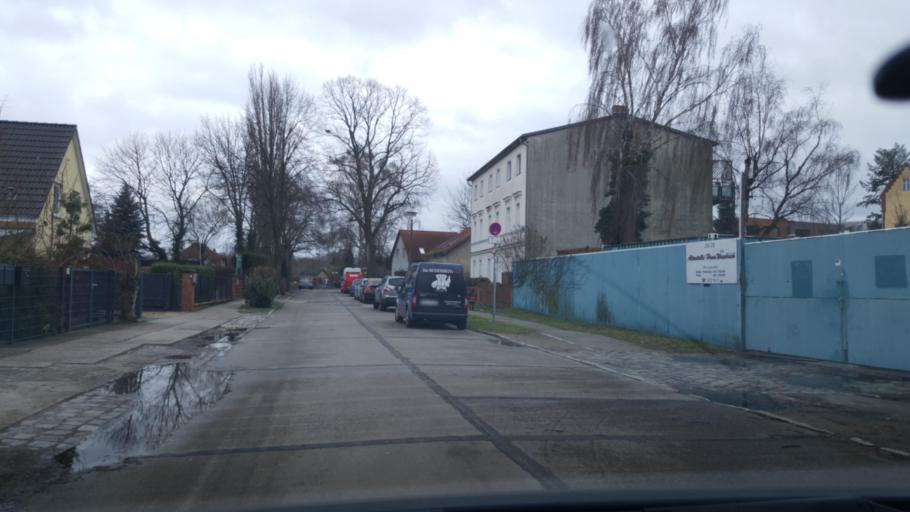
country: DE
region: Berlin
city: Altglienicke
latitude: 52.4208
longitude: 13.5421
